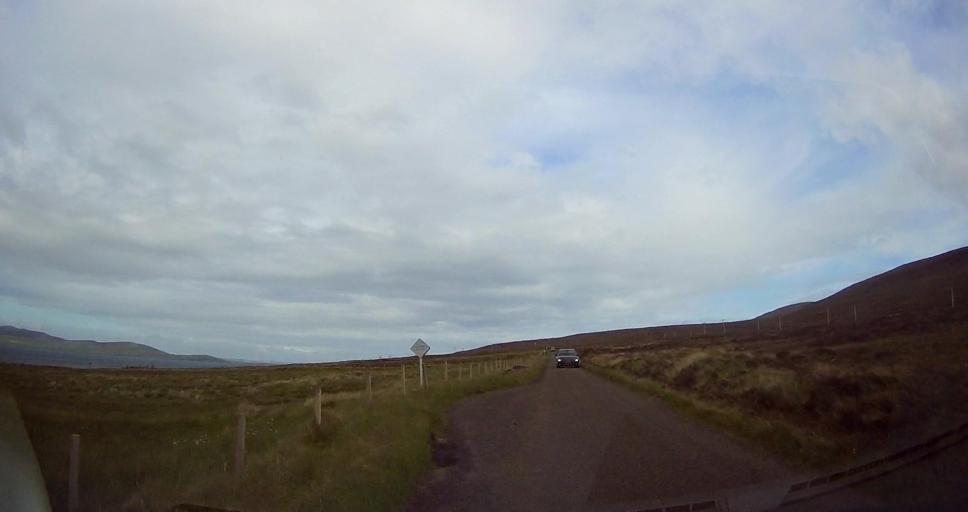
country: GB
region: Scotland
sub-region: Orkney Islands
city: Stromness
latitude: 58.9027
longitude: -3.2984
